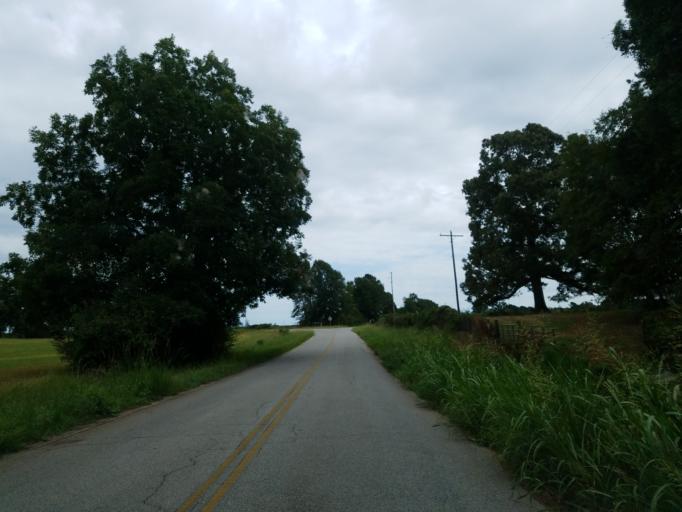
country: US
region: Georgia
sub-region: Monroe County
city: Forsyth
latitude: 32.9897
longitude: -84.0432
